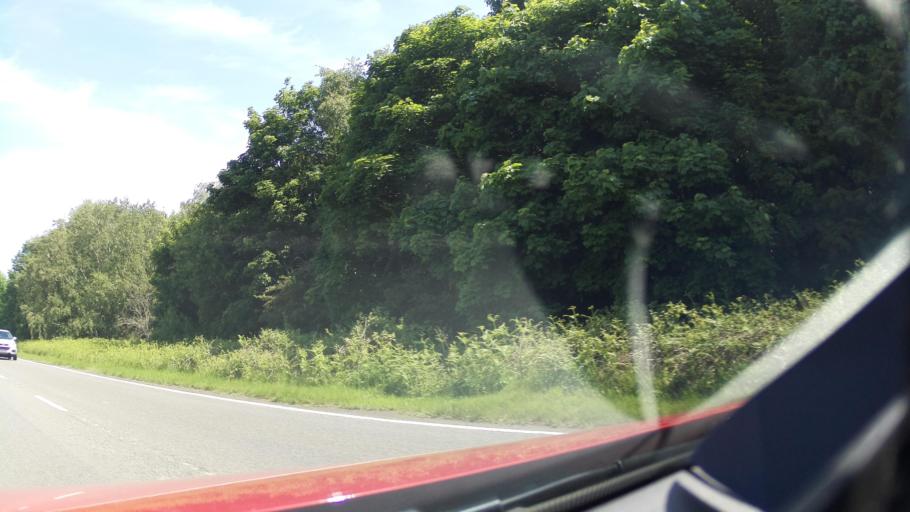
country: GB
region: England
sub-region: North Lincolnshire
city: Manton
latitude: 53.5228
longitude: -0.5797
